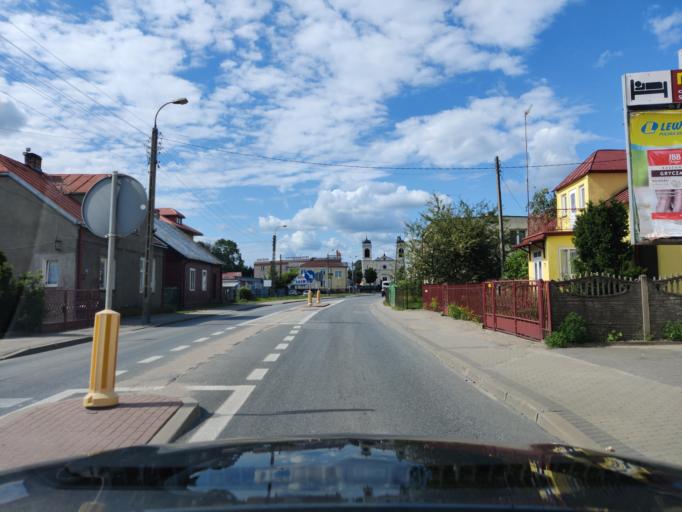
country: PL
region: Podlasie
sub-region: Powiat wysokomazowiecki
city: Czyzew
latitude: 52.7965
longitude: 22.3130
